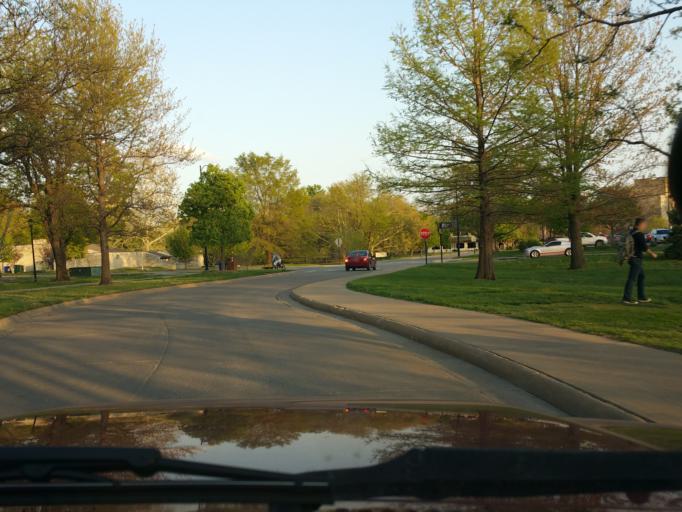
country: US
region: Kansas
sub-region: Riley County
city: Manhattan
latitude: 39.1949
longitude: -96.5813
